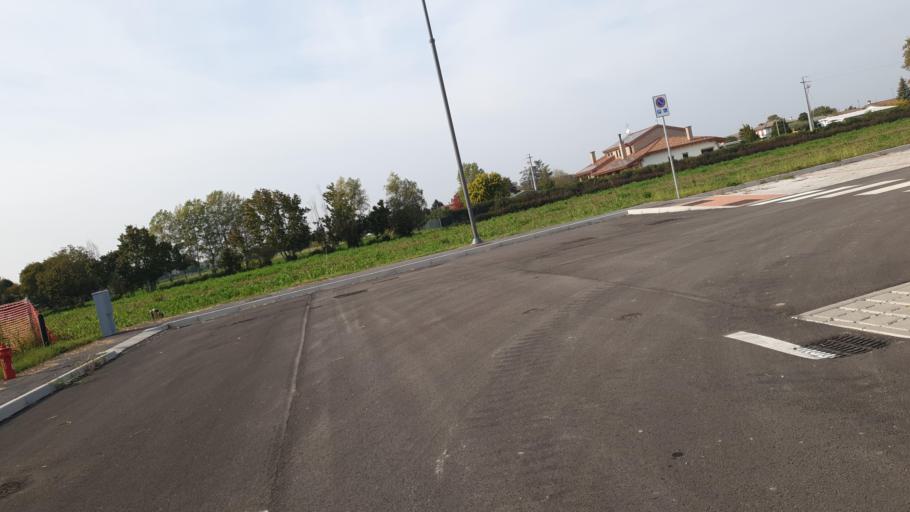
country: IT
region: Veneto
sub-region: Provincia di Padova
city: Albignasego
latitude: 45.3379
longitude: 11.9004
